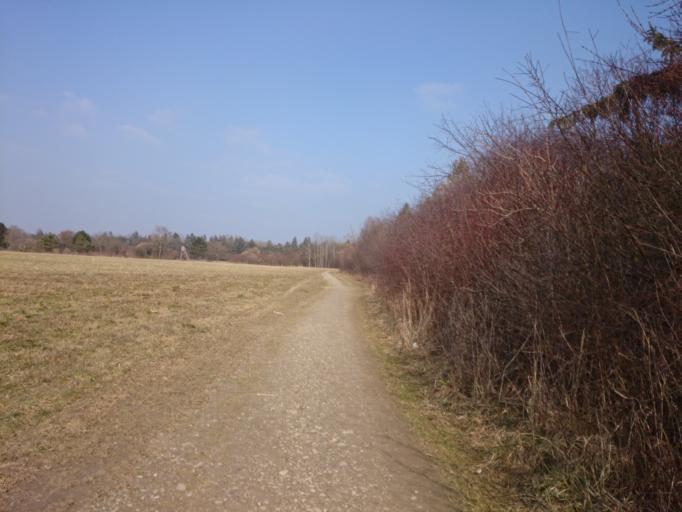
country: DE
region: Bavaria
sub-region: Swabia
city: Konigsbrunn
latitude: 48.2824
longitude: 10.9080
